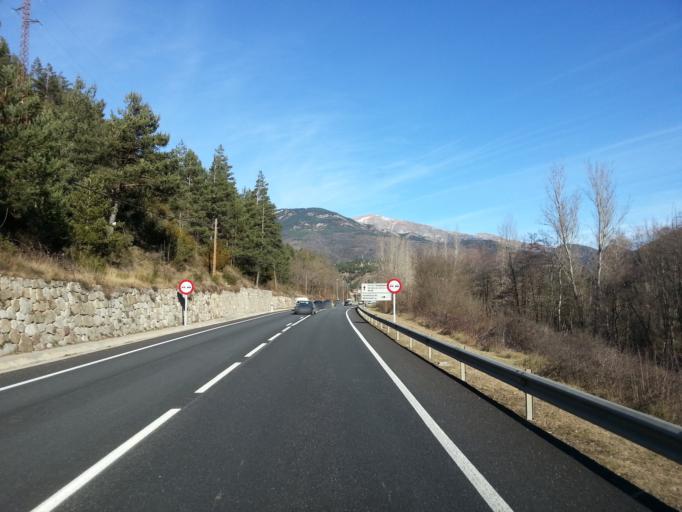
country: ES
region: Catalonia
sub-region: Provincia de Barcelona
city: Guardiola de Bergueda
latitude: 42.2250
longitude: 1.8736
